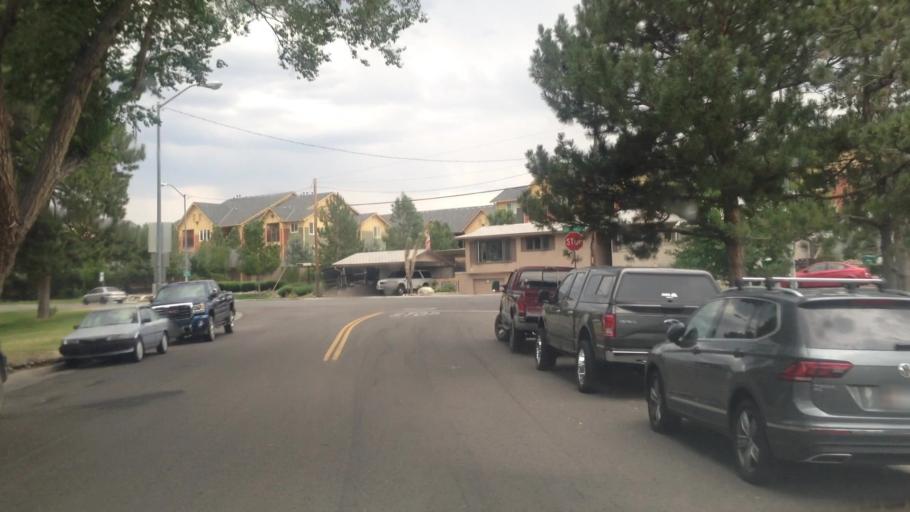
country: US
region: Nevada
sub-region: Washoe County
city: Reno
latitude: 39.5203
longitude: -119.8316
